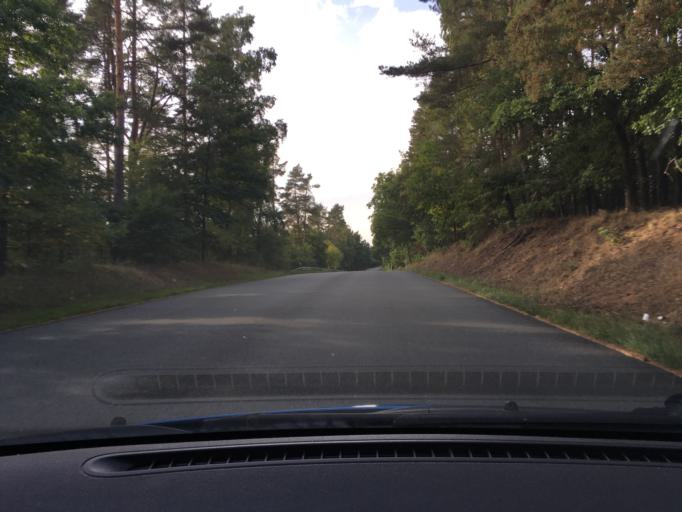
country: DE
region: Lower Saxony
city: Munster
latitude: 52.9100
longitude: 10.0892
